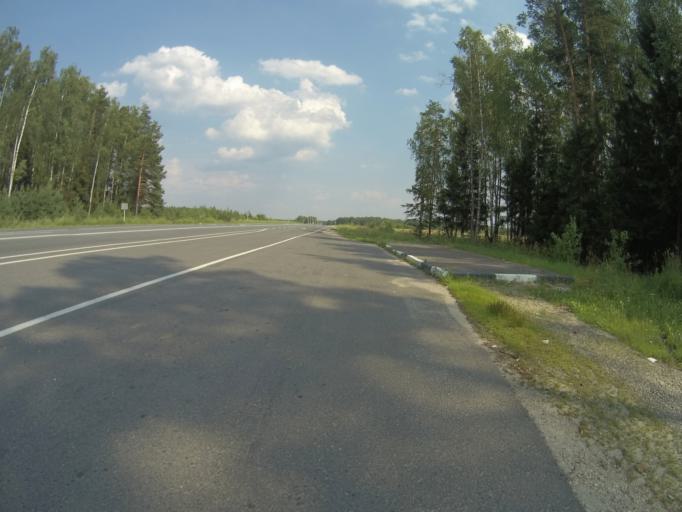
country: RU
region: Vladimir
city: Andreyevo
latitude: 55.9374
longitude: 41.0696
